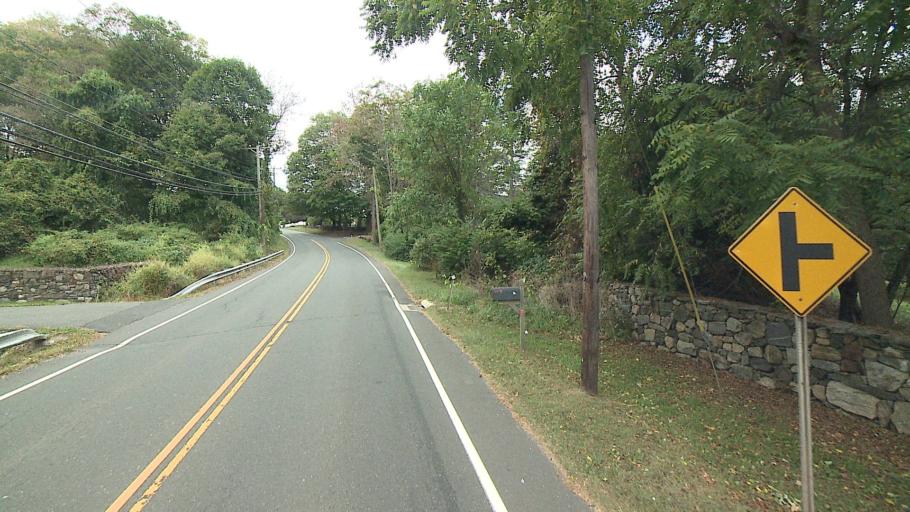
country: US
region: Connecticut
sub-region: Fairfield County
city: Wilton
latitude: 41.2029
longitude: -73.4495
